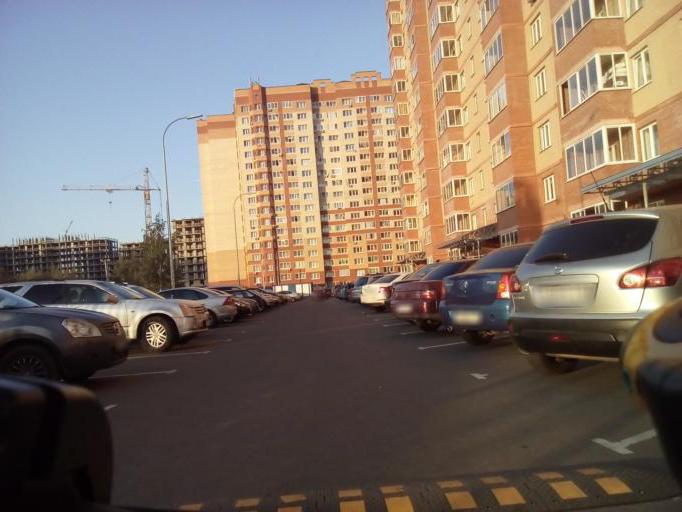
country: RU
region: Moskovskaya
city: Ramenskoye
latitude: 55.5924
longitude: 38.2519
